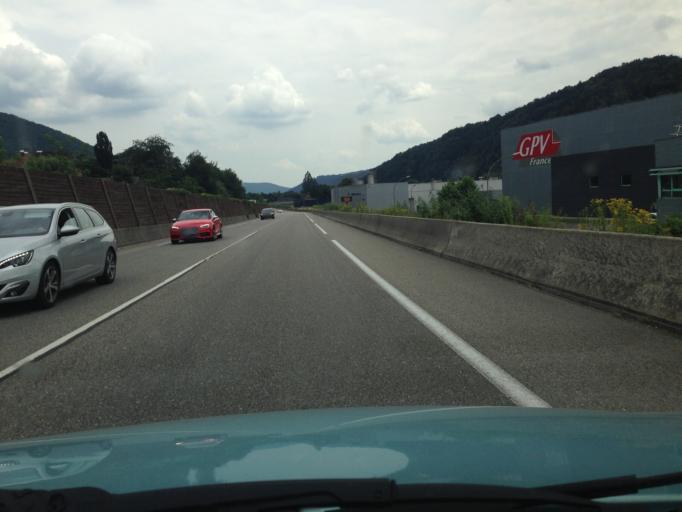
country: FR
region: Alsace
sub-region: Departement du Haut-Rhin
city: Saint-Amarin
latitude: 47.8769
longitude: 7.0216
